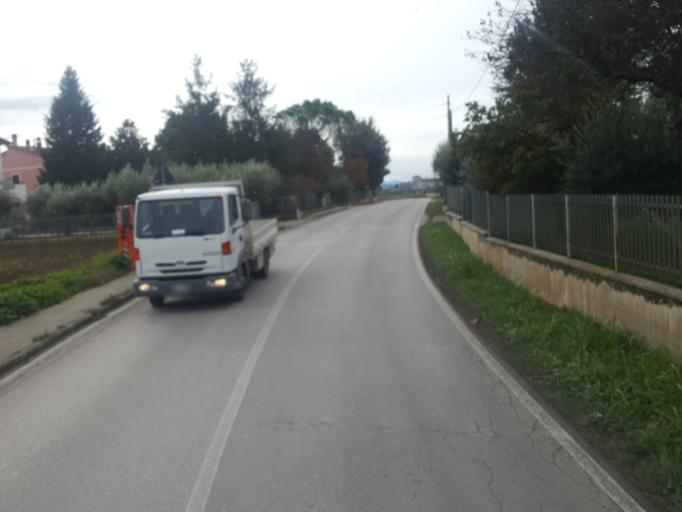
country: IT
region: Umbria
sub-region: Provincia di Perugia
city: San Martino in Campo
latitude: 43.0716
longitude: 12.4264
